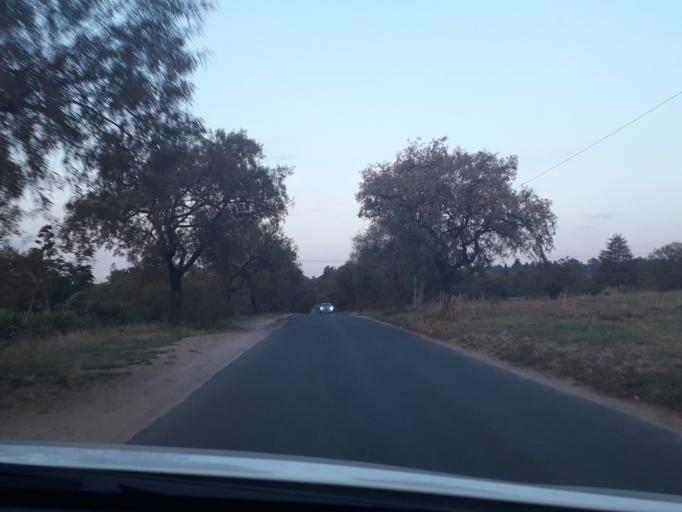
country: ZA
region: Gauteng
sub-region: City of Johannesburg Metropolitan Municipality
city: Diepsloot
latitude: -25.9870
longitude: 28.0488
